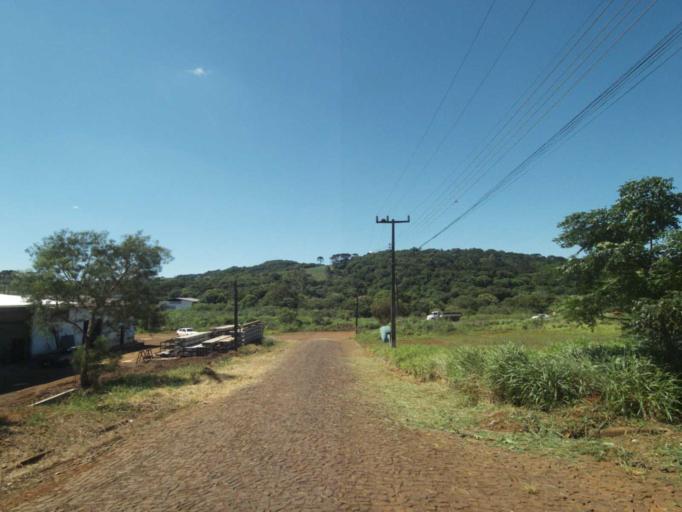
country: BR
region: Parana
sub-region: Laranjeiras Do Sul
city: Laranjeiras do Sul
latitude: -25.3800
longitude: -52.2084
